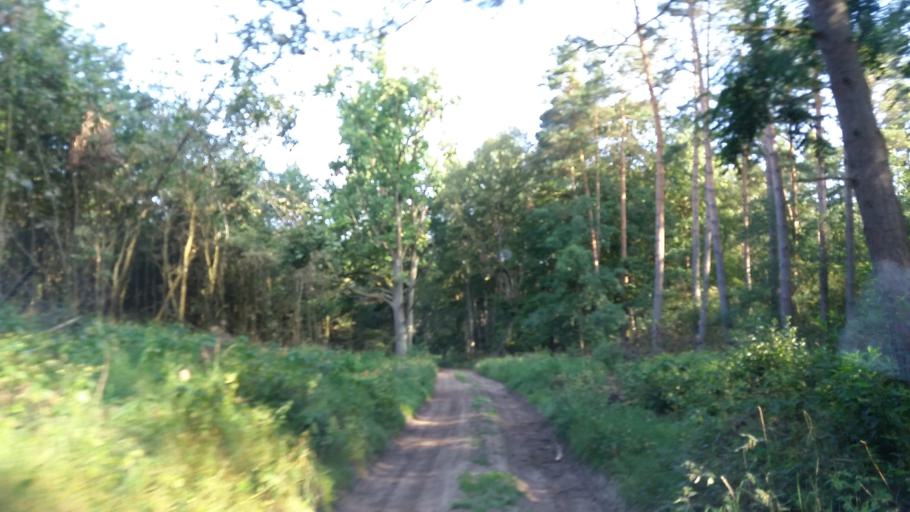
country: PL
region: West Pomeranian Voivodeship
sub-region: Powiat choszczenski
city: Recz
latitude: 53.1979
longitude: 15.5425
